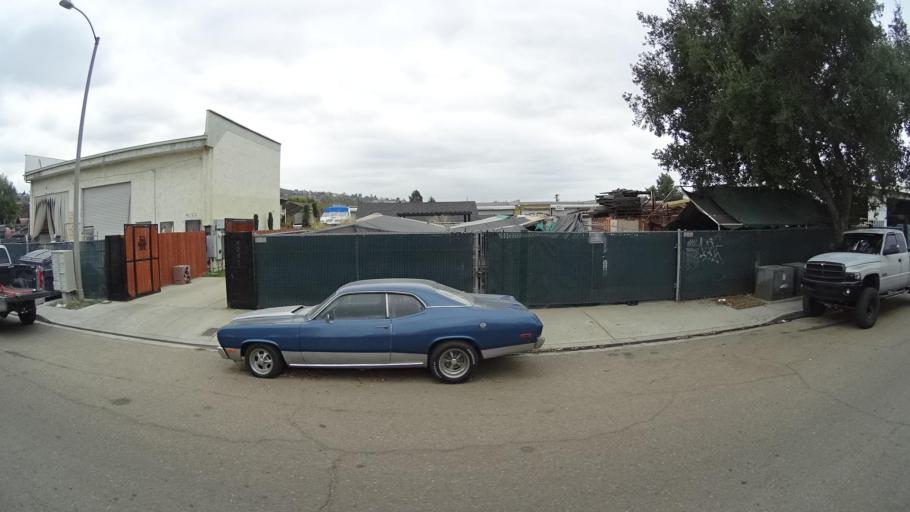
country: US
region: California
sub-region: San Diego County
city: Spring Valley
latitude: 32.7420
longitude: -117.0036
